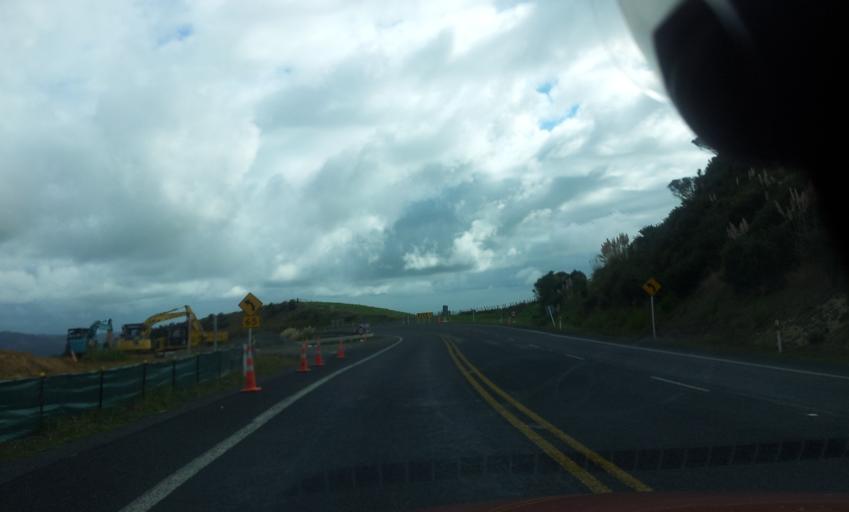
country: NZ
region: Northland
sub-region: Whangarei
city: Ruakaka
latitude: -36.0561
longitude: 174.4258
